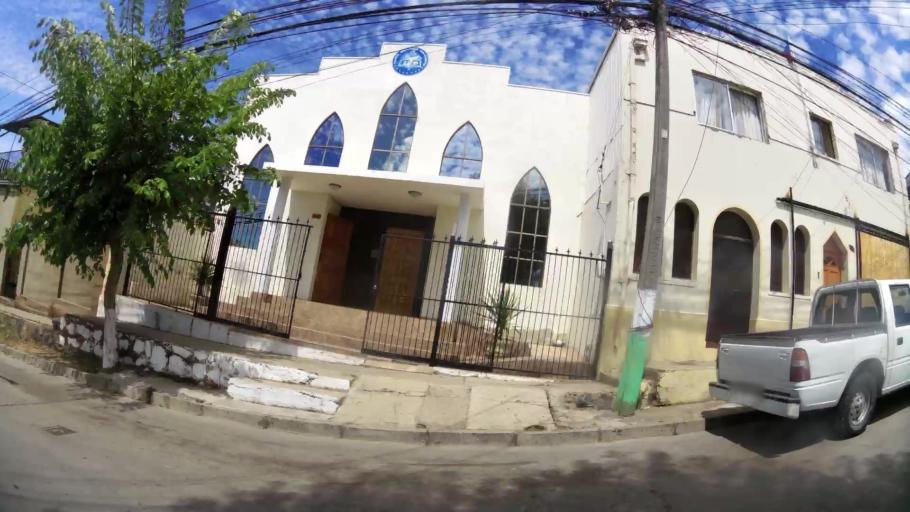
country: CL
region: Valparaiso
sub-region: Provincia de Valparaiso
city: Vina del Mar
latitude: -33.0358
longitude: -71.5843
